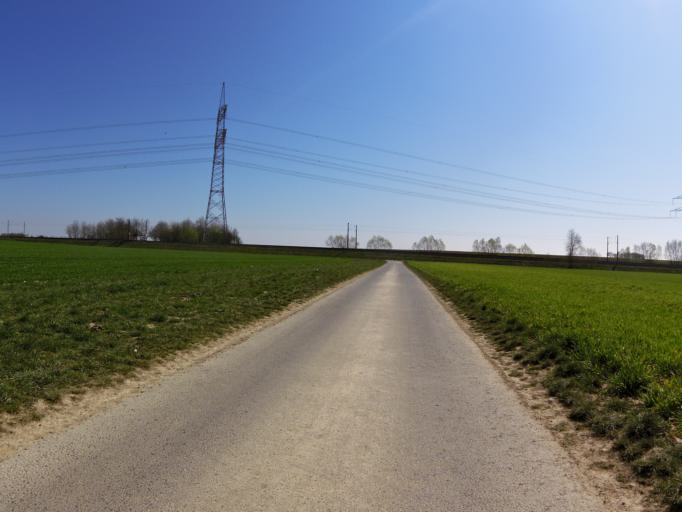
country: DE
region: Bavaria
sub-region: Regierungsbezirk Unterfranken
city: Oberpleichfeld
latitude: 49.8324
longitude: 10.0862
